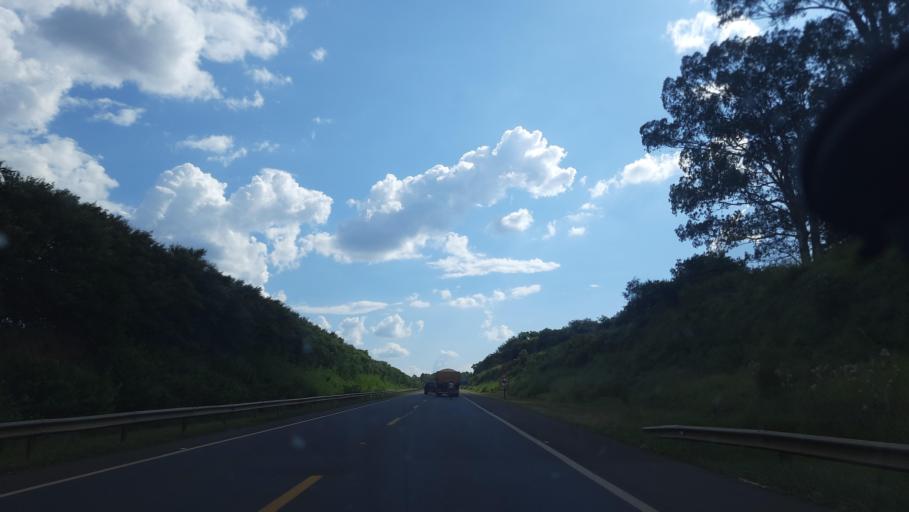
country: BR
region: Sao Paulo
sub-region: Casa Branca
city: Casa Branca
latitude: -21.7518
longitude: -46.9960
